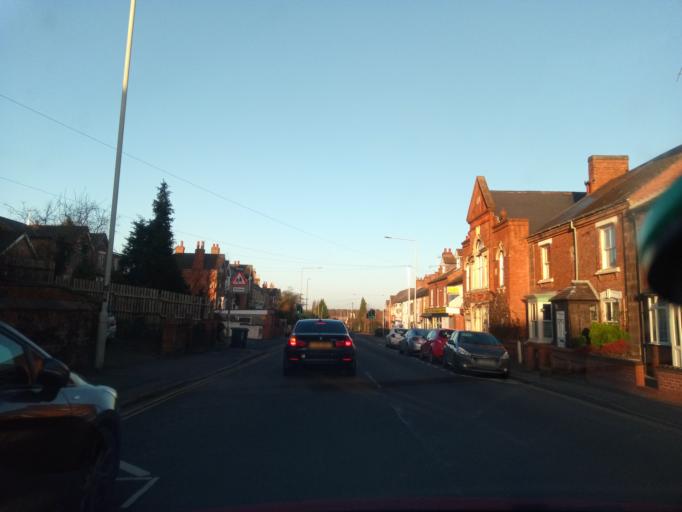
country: GB
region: England
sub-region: Leicestershire
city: Kegworth
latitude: 52.8368
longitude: -1.2801
